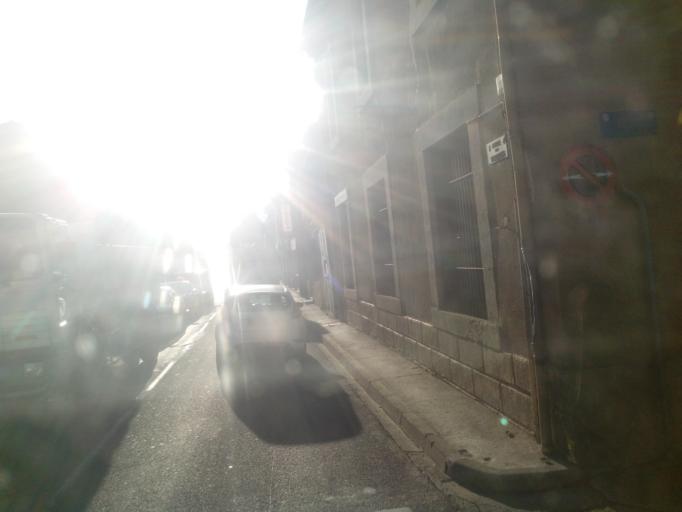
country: FR
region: Languedoc-Roussillon
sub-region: Departement de l'Aude
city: Couiza
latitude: 42.9430
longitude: 2.2555
